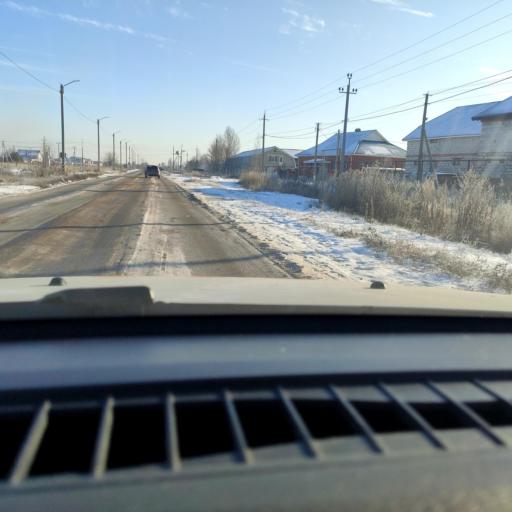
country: RU
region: Samara
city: Podstepki
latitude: 53.5229
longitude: 49.1507
